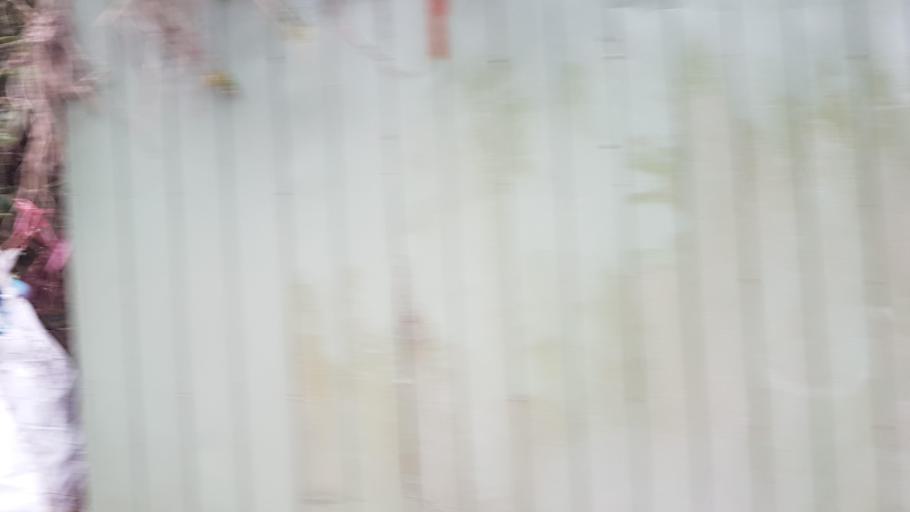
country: TW
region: Taiwan
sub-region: Chiayi
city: Jiayi Shi
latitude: 23.3263
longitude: 120.4873
